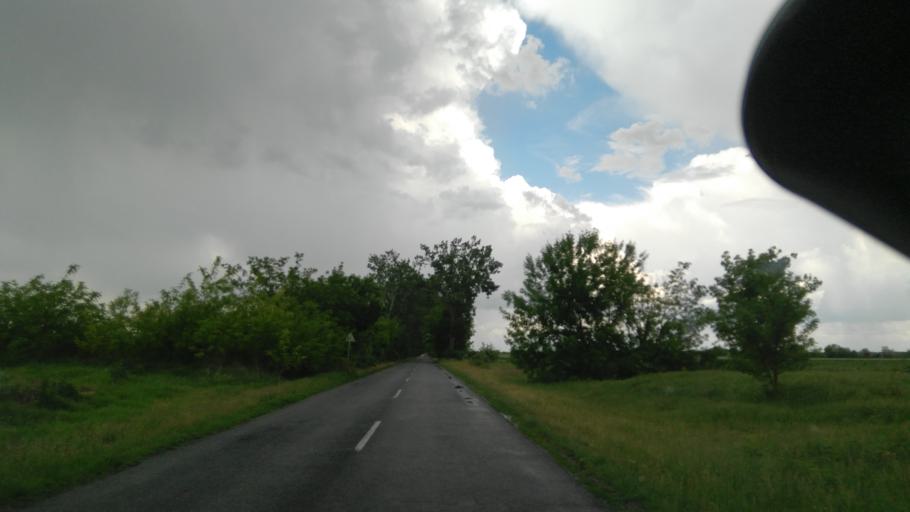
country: HU
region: Bekes
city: Fuzesgyarmat
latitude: 47.1365
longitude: 21.1551
